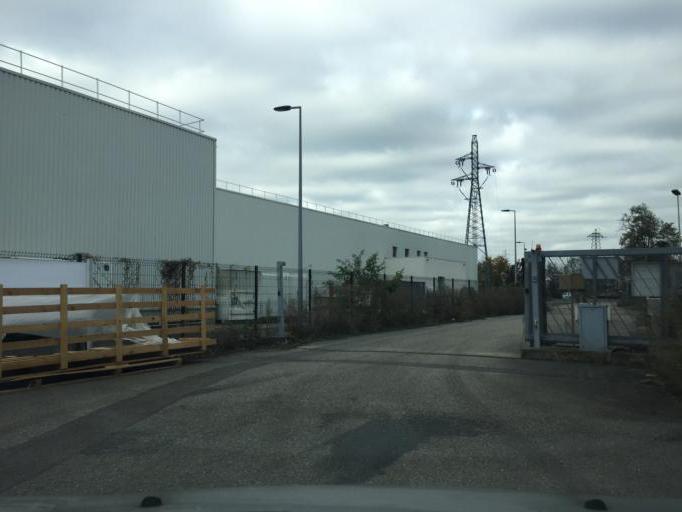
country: FR
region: Rhone-Alpes
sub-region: Departement de l'Ain
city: Jassans-Riottier
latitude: 45.9828
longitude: 4.7449
